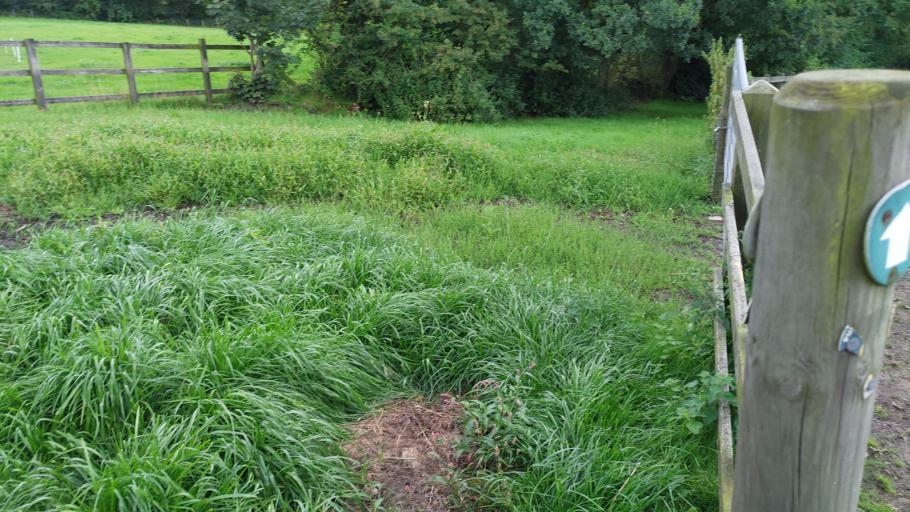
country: GB
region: England
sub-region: Lancashire
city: Coppull
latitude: 53.6341
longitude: -2.6586
